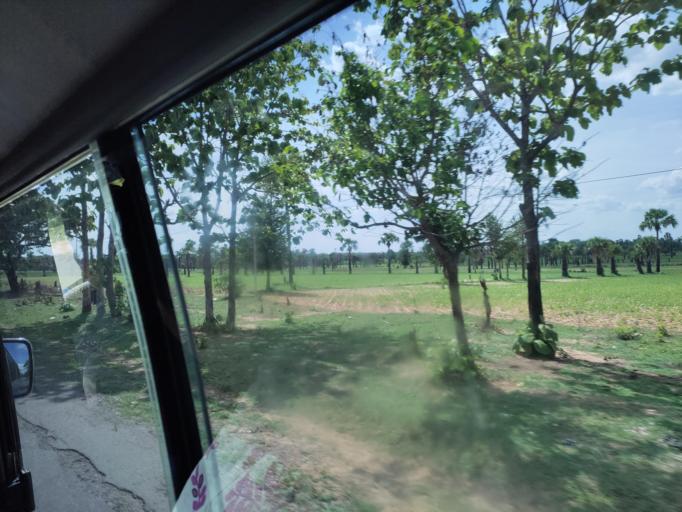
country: MM
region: Magway
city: Chauk
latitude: 20.8203
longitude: 95.0669
